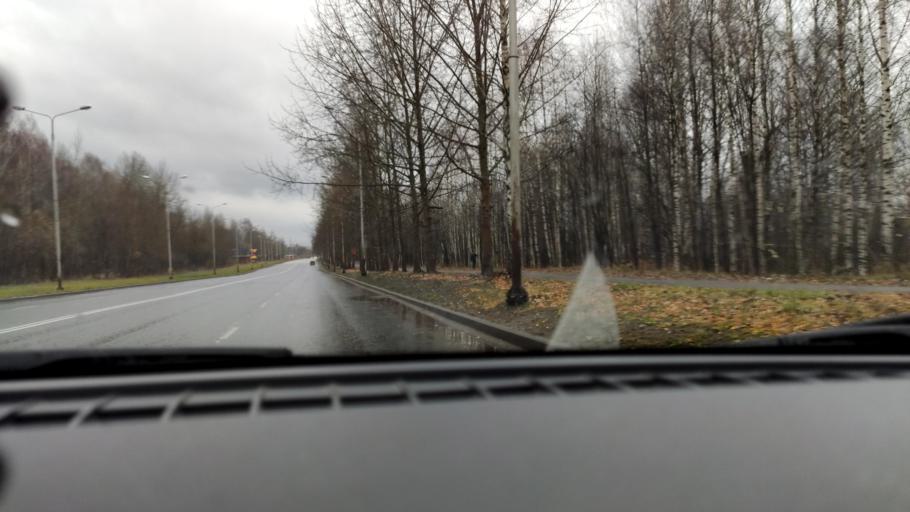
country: RU
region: Perm
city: Perm
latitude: 58.1061
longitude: 56.3944
